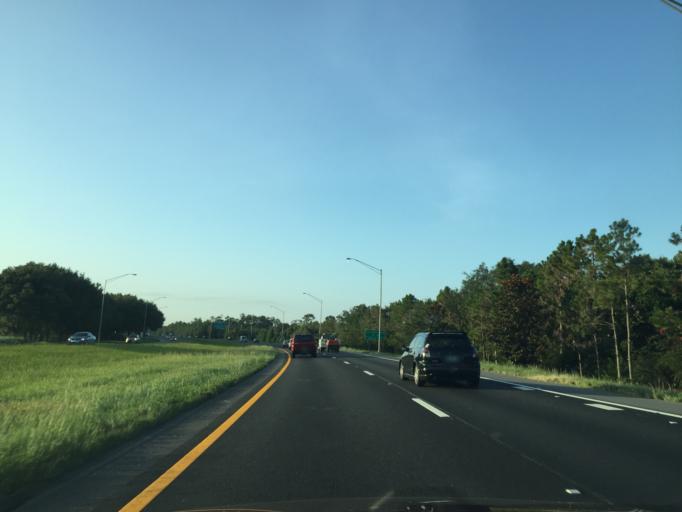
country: US
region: Florida
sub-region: Seminole County
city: Goldenrod
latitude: 28.6101
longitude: -81.2583
